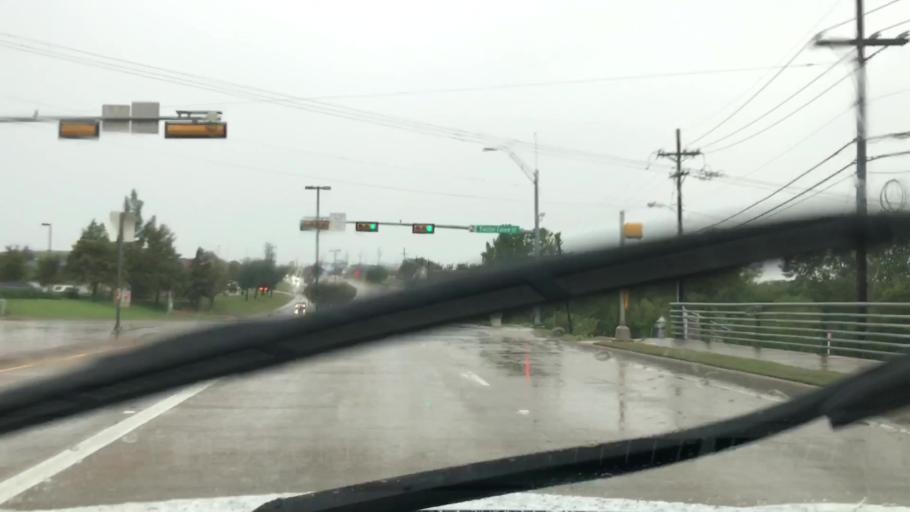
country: US
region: Texas
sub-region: Rockwall County
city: Rockwall
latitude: 32.9018
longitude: -96.4662
